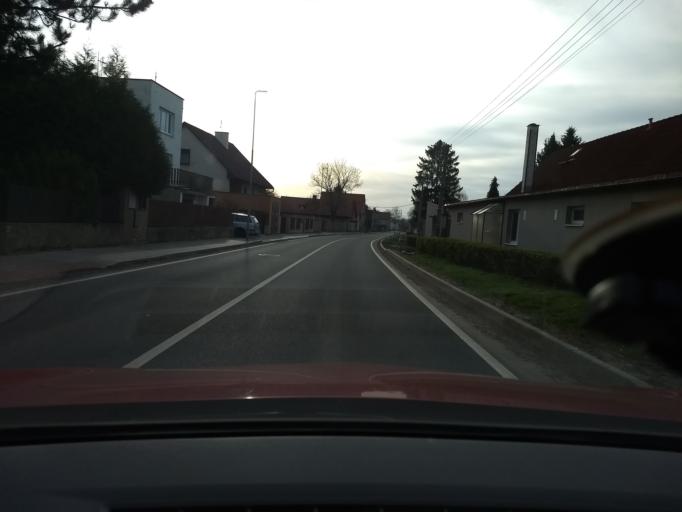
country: CZ
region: Central Bohemia
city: Jenec
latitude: 50.0521
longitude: 14.1735
